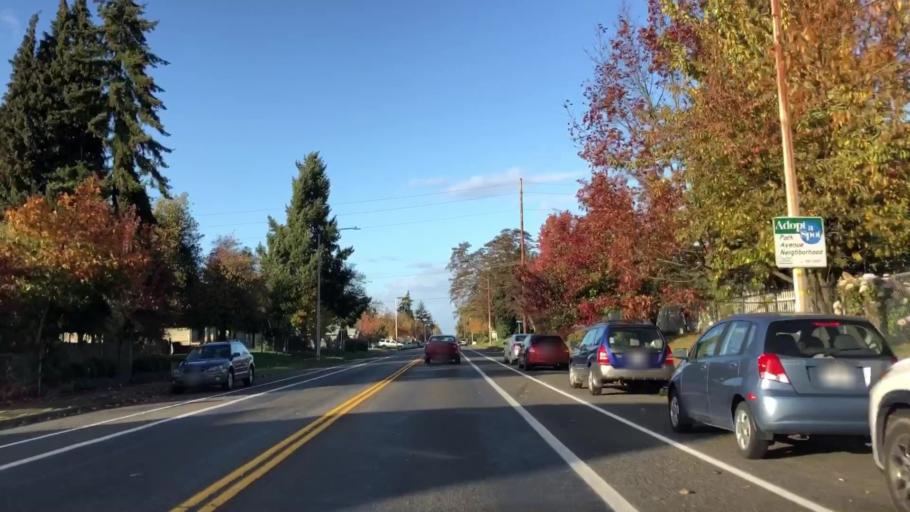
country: US
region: Washington
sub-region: Pierce County
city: Parkland
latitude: 47.2008
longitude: -122.4432
